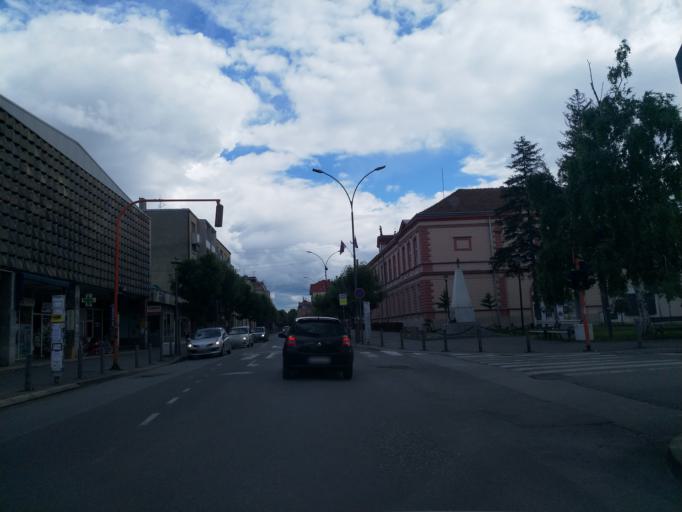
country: RS
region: Central Serbia
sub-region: Pomoravski Okrug
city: Cuprija
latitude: 43.9334
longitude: 21.3708
